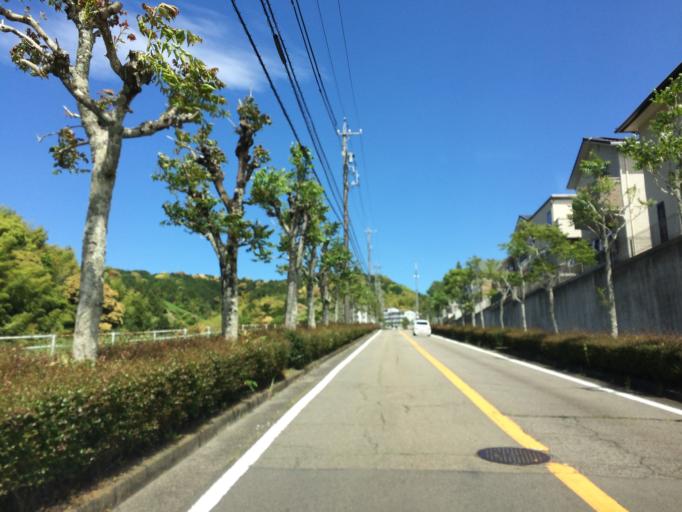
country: JP
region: Shizuoka
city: Fujieda
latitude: 34.8559
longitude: 138.2306
